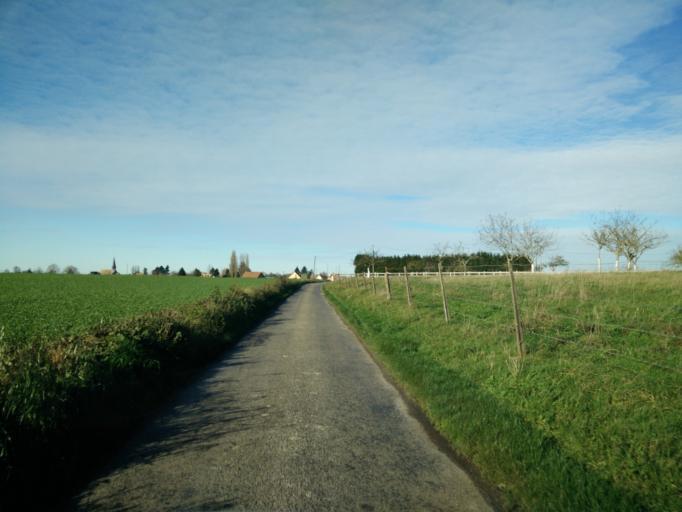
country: FR
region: Haute-Normandie
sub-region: Departement de l'Eure
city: Saint-Pierre-des-Fleurs
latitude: 49.1781
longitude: 0.9871
